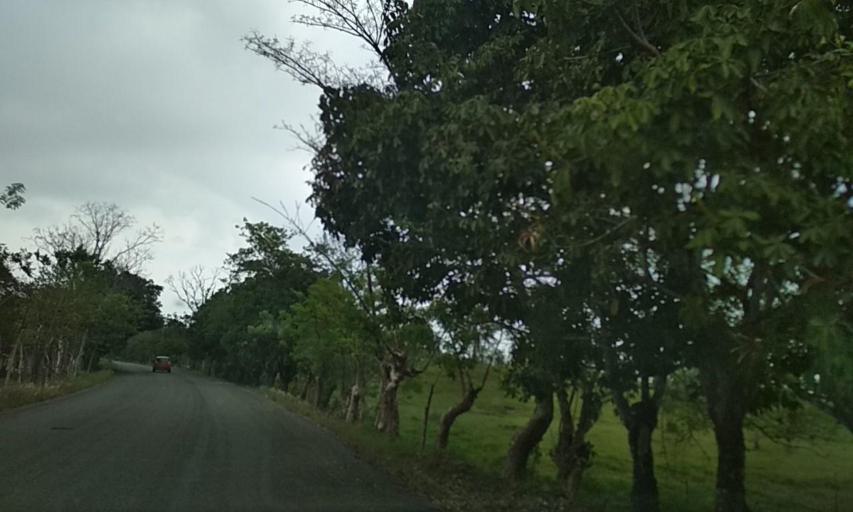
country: MX
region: Tabasco
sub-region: Huimanguillo
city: Francisco Rueda
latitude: 17.5762
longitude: -94.1009
